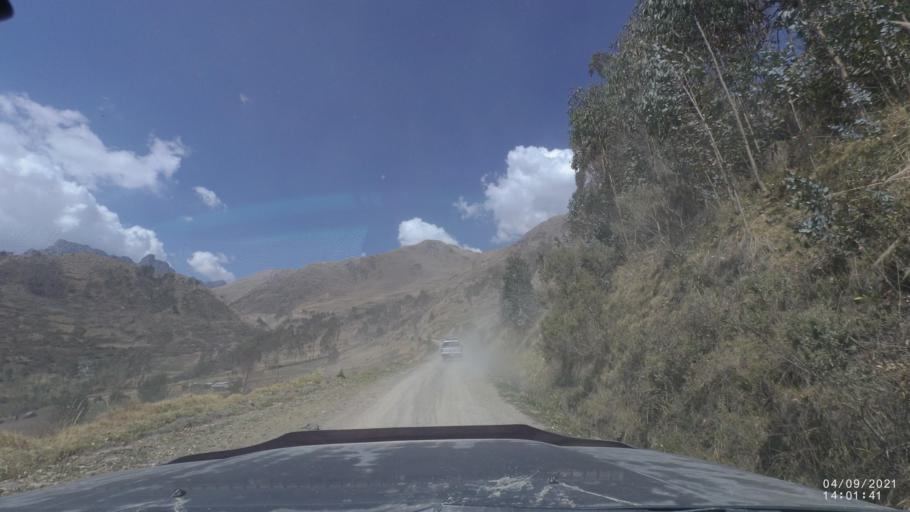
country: BO
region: Cochabamba
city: Sipe Sipe
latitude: -17.2330
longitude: -66.4841
